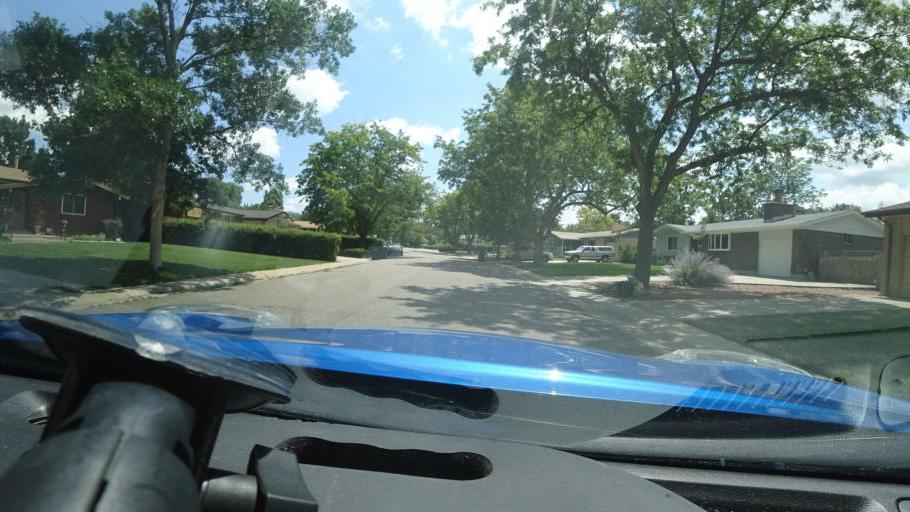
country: US
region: Colorado
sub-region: Adams County
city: Aurora
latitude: 39.7048
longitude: -104.8421
